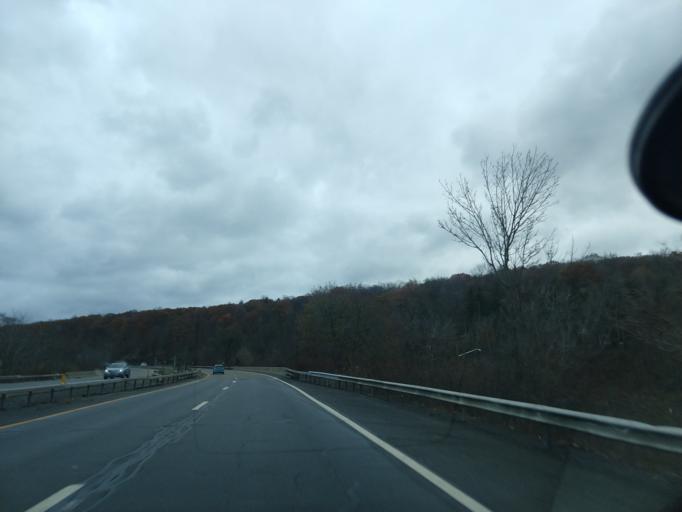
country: US
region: New York
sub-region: Tompkins County
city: Cayuga Heights
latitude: 42.4627
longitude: -76.4992
